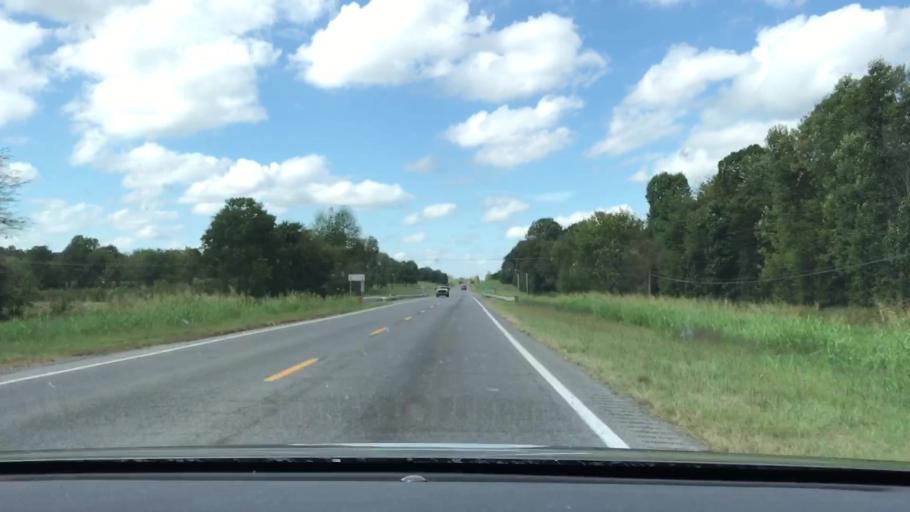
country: US
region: Kentucky
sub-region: Livingston County
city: Ledbetter
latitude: 37.0075
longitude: -88.4817
